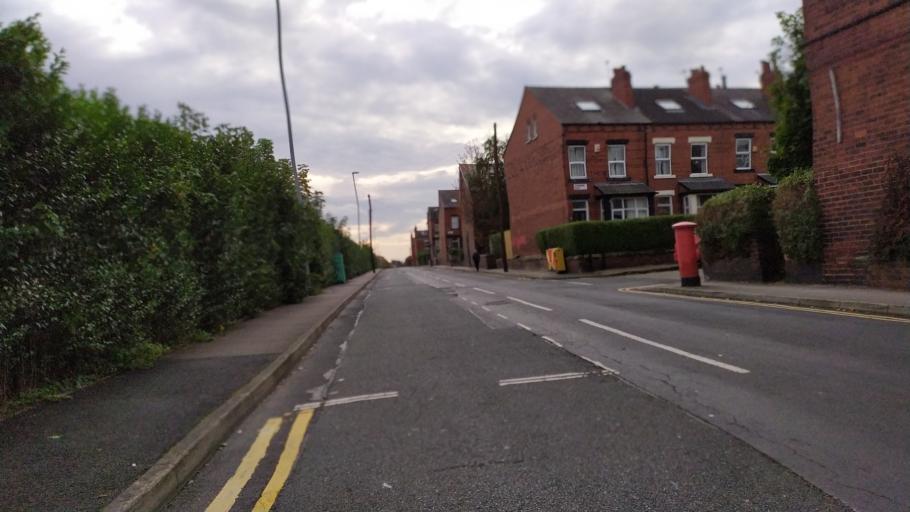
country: GB
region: England
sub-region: City and Borough of Leeds
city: Leeds
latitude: 53.8142
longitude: -1.5837
